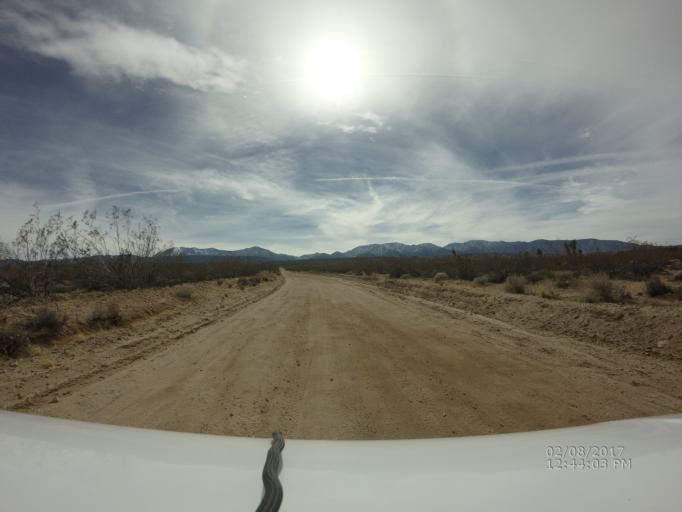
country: US
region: California
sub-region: Los Angeles County
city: Lake Los Angeles
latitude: 34.4871
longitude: -117.8178
